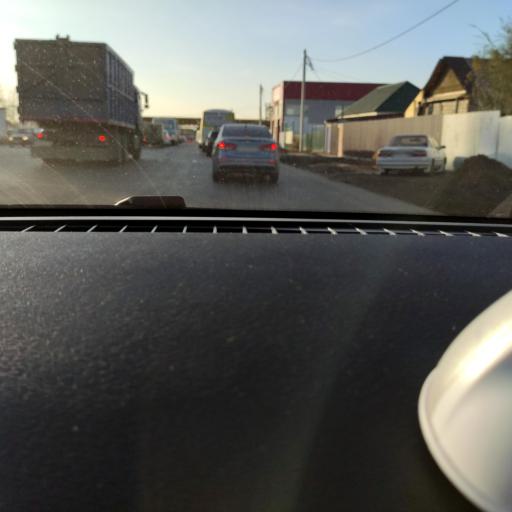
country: RU
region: Samara
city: Samara
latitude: 53.1359
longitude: 50.1064
